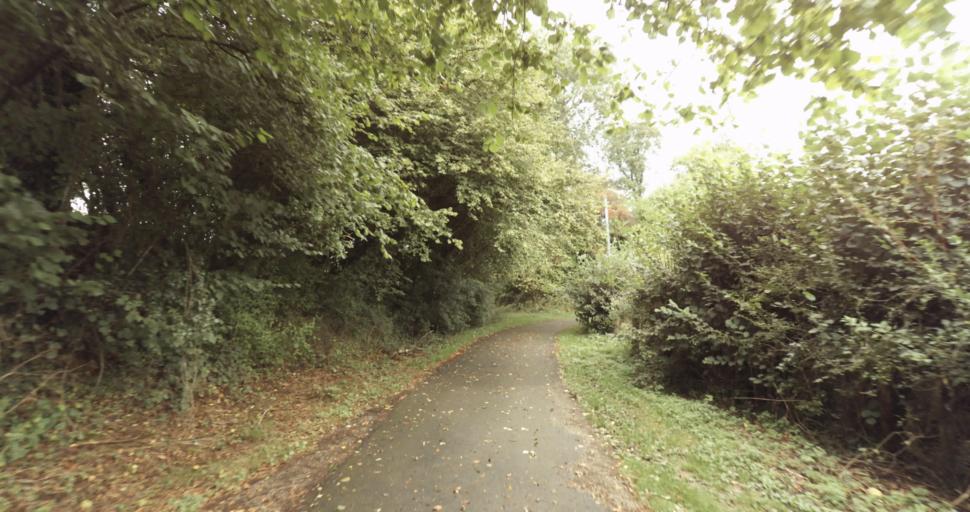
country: FR
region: Lower Normandy
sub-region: Departement de l'Orne
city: Sainte-Gauburge-Sainte-Colombe
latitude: 48.7338
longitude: 0.4153
